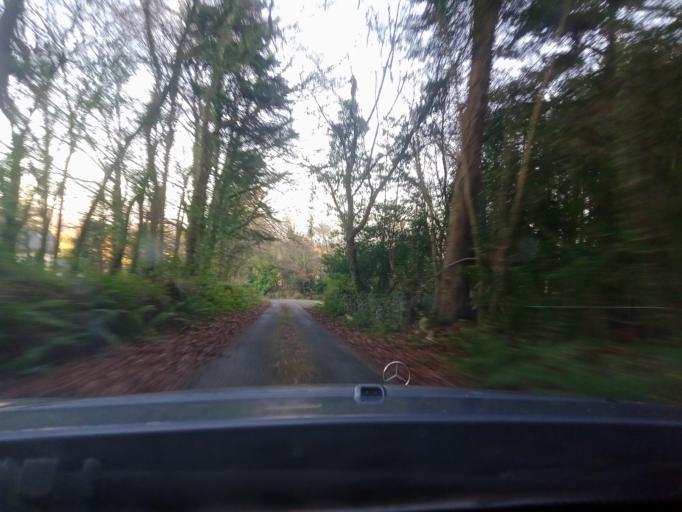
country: IE
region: Leinster
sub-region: Kilkenny
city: Graiguenamanagh
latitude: 52.4720
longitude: -6.9379
